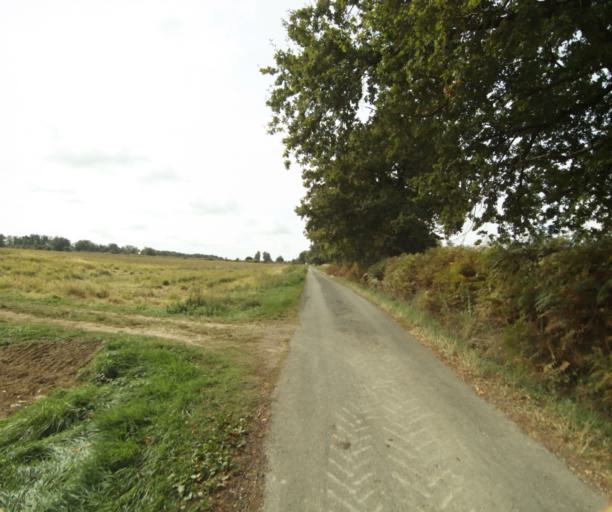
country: FR
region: Midi-Pyrenees
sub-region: Departement du Gers
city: Eauze
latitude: 43.8256
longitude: 0.1147
